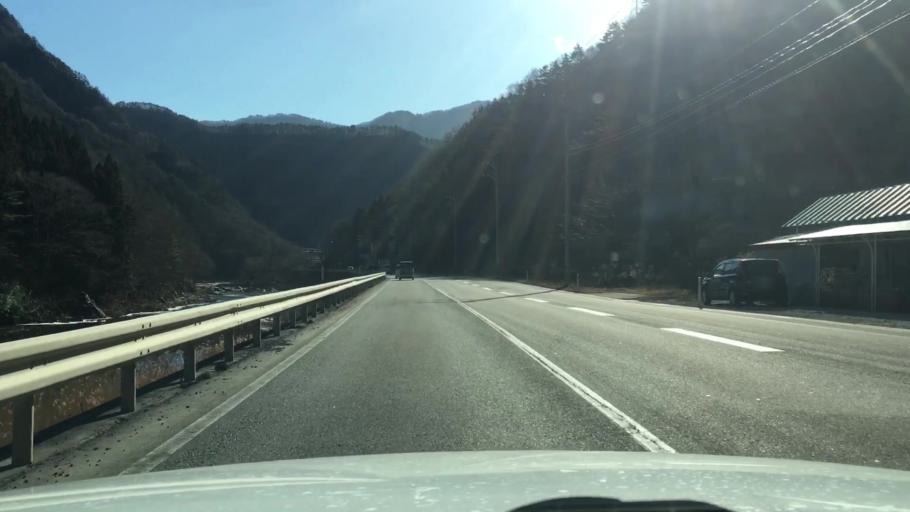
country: JP
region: Iwate
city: Miyako
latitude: 39.6149
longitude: 141.7887
